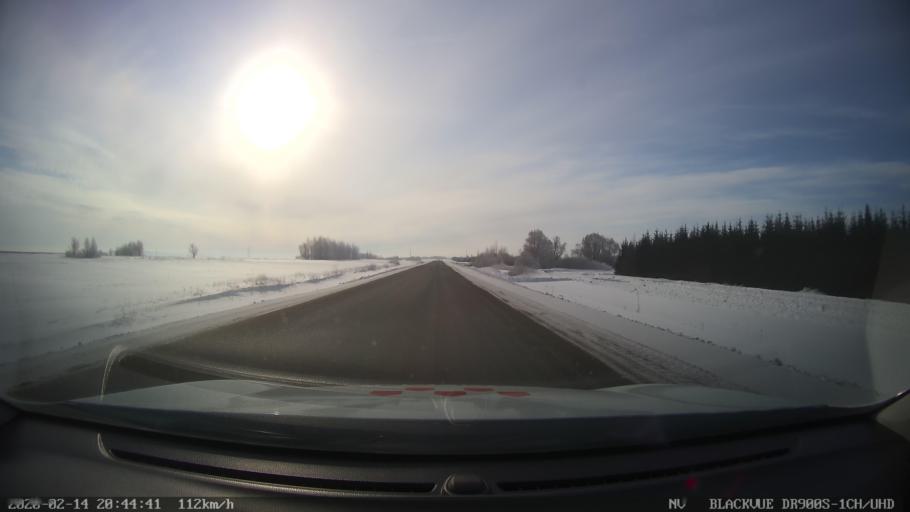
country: RU
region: Tatarstan
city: Kuybyshevskiy Zaton
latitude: 55.2896
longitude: 49.1453
